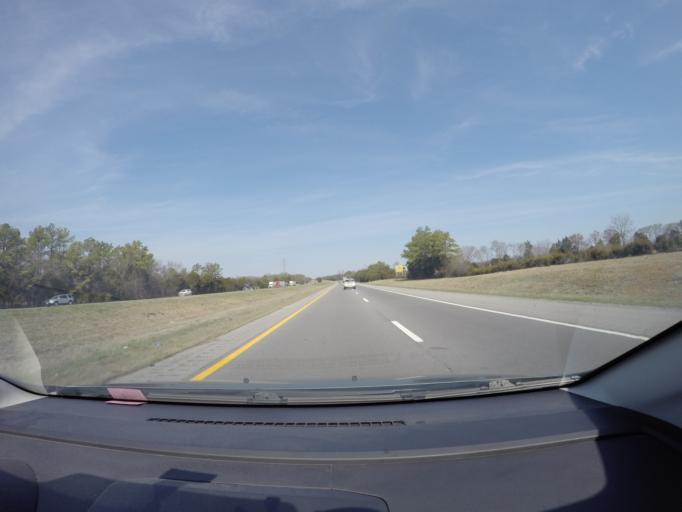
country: US
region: Tennessee
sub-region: Rutherford County
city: Plainview
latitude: 35.7483
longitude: -86.3409
